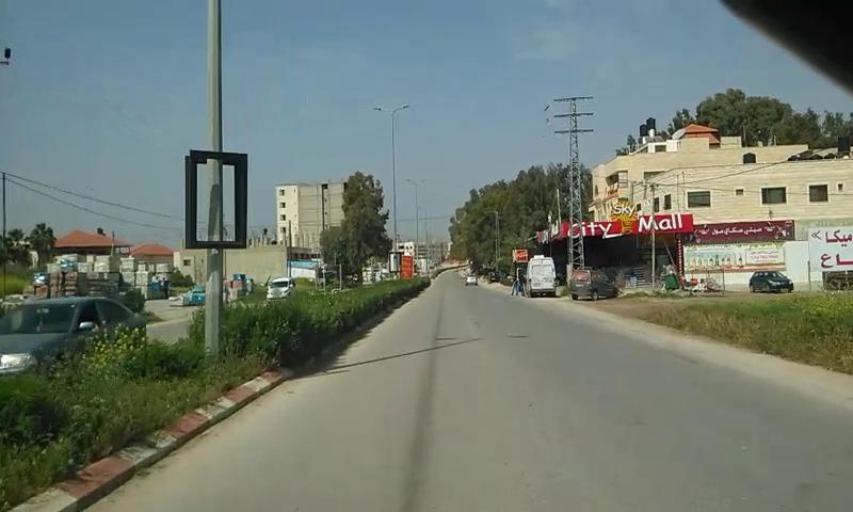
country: PS
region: West Bank
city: Janin
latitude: 32.4783
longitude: 35.3001
